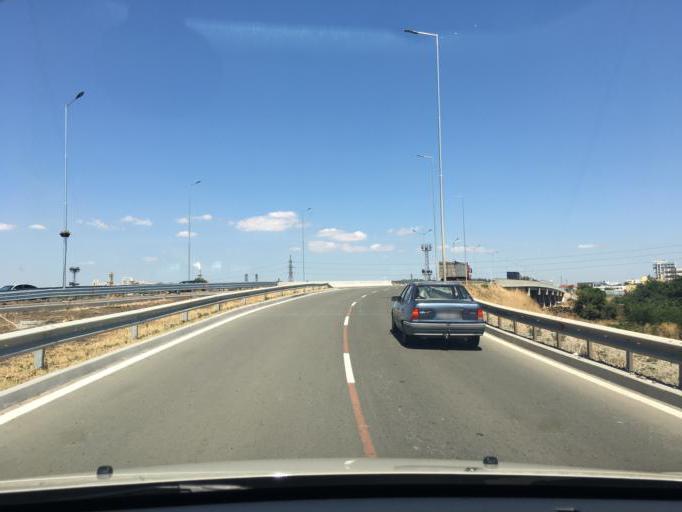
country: BG
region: Burgas
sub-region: Obshtina Burgas
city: Burgas
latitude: 42.5130
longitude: 27.4356
